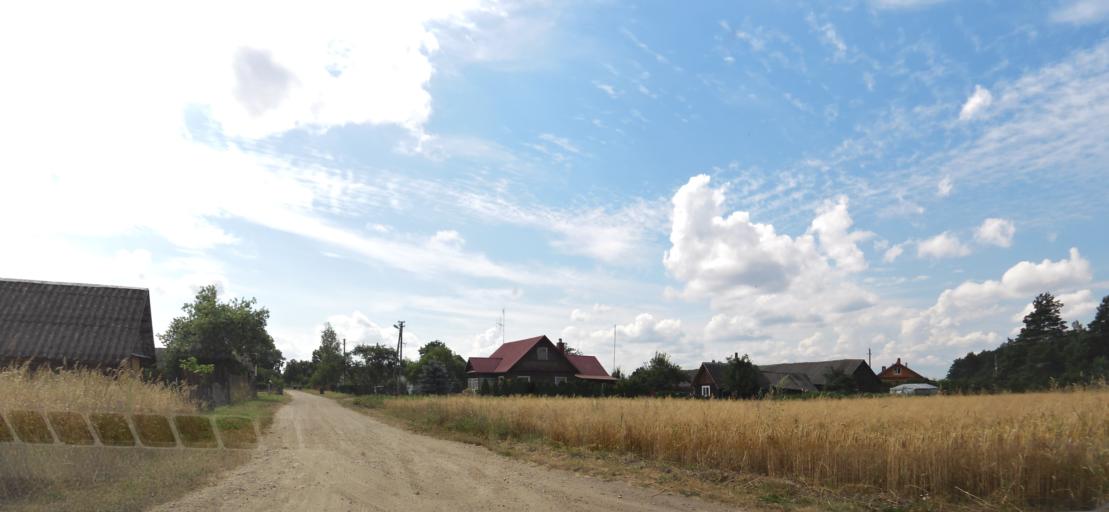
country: LT
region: Vilnius County
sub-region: Trakai
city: Rudiskes
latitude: 54.2997
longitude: 24.7855
